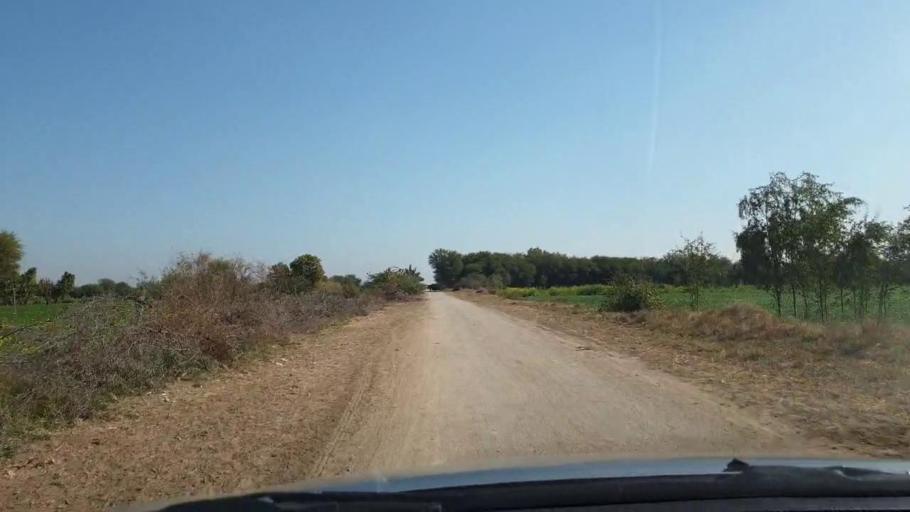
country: PK
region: Sindh
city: Jhol
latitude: 25.9246
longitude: 68.9342
